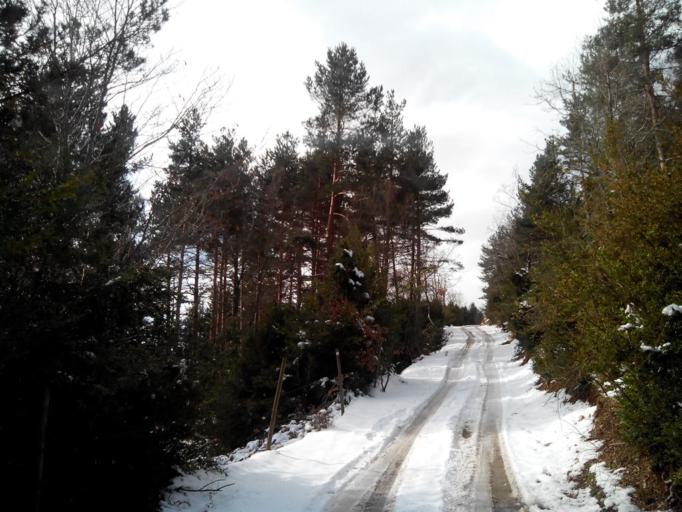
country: ES
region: Catalonia
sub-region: Provincia de Barcelona
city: Vilada
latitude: 42.1864
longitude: 1.9341
